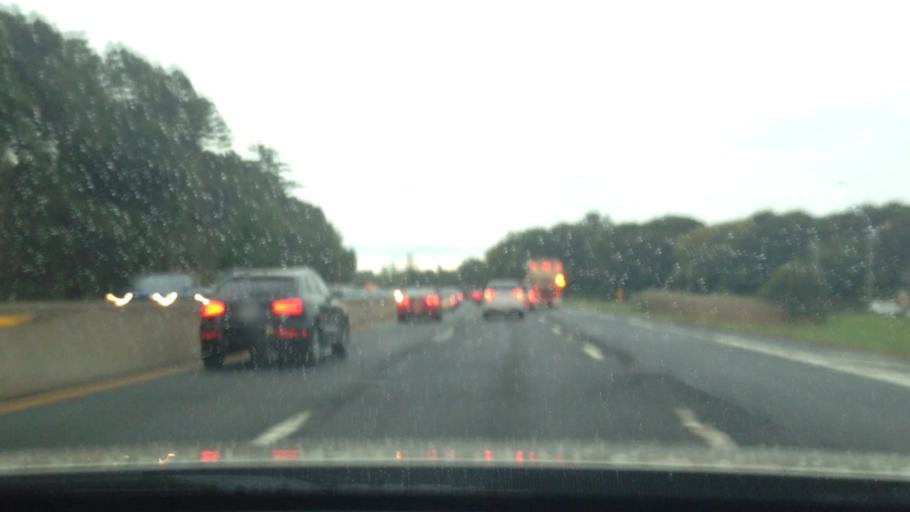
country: US
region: New York
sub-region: Suffolk County
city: North Great River
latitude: 40.7481
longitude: -73.1547
